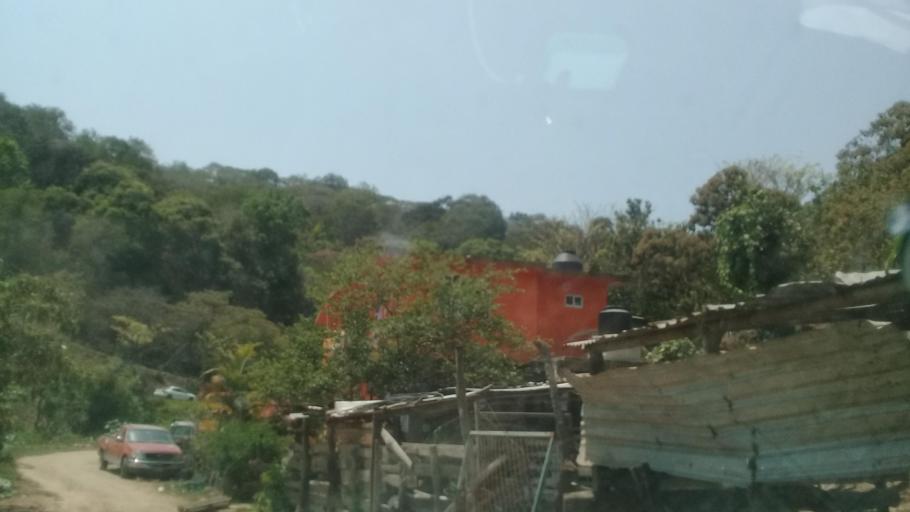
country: MX
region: Veracruz
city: El Castillo
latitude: 19.5570
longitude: -96.8574
